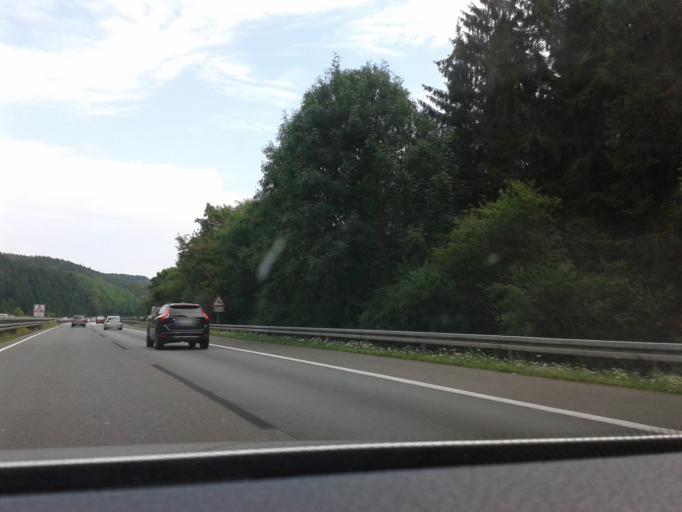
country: DE
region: North Rhine-Westphalia
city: Marsberg
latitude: 51.5212
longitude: 8.9259
